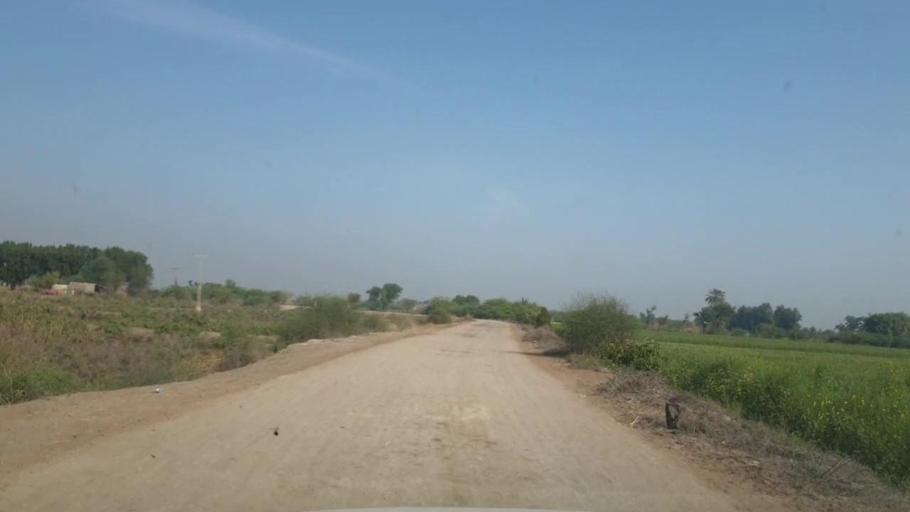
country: PK
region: Sindh
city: Mirpur Khas
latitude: 25.5096
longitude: 69.0391
